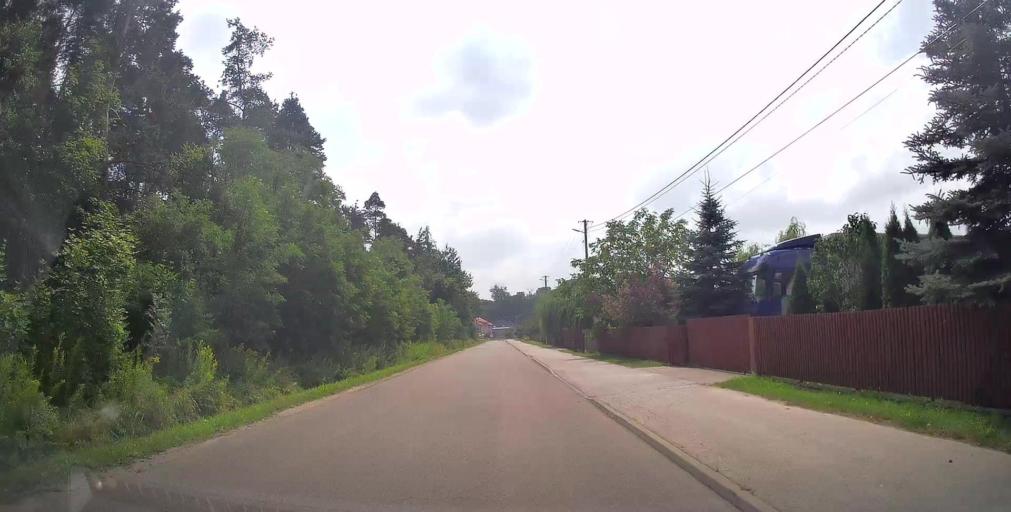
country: PL
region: Masovian Voivodeship
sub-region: Powiat bialobrzeski
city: Sucha
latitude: 51.6248
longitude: 20.9530
